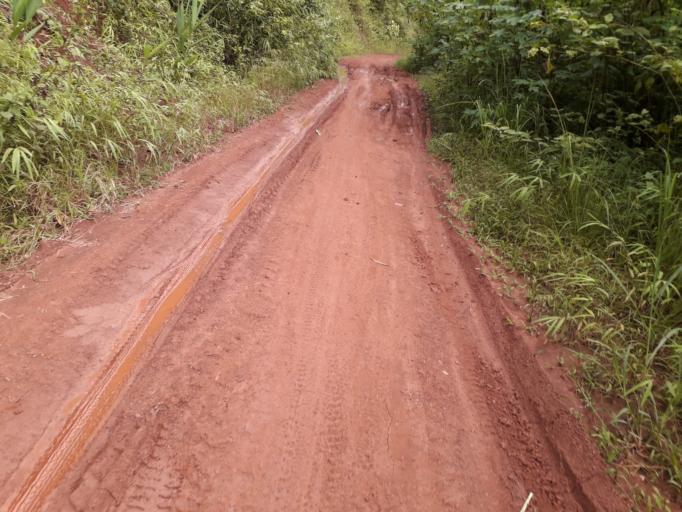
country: CN
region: Yunnan
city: Menglie
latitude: 22.2409
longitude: 101.6139
